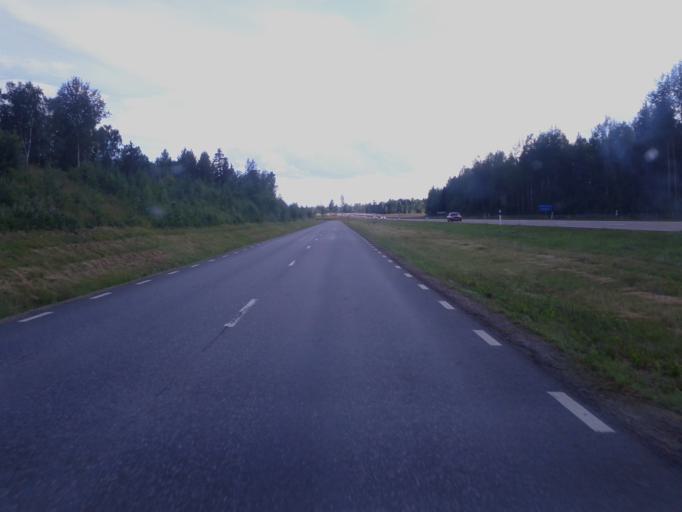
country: SE
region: Dalarna
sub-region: Borlange Kommun
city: Ornas
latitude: 60.5088
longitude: 15.5313
